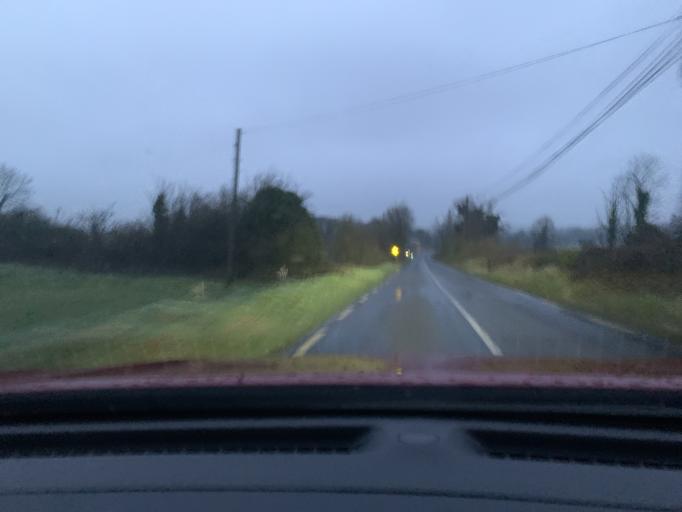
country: IE
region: Connaught
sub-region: Sligo
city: Ballymote
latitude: 54.0045
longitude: -8.5218
